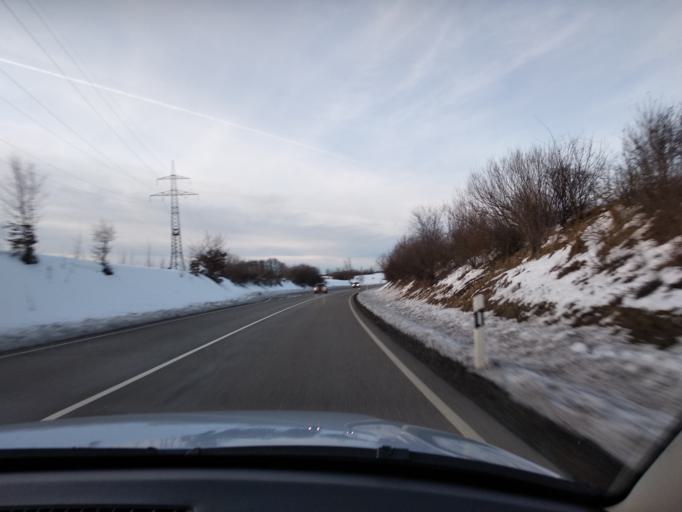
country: DE
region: Bavaria
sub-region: Upper Bavaria
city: Zorneding
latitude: 48.0771
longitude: 11.8120
